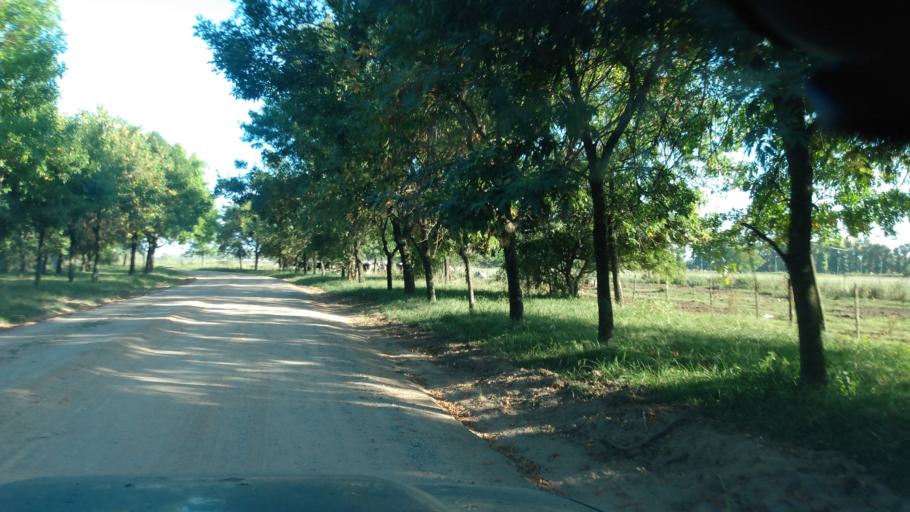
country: AR
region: Buenos Aires
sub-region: Partido de Lujan
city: Lujan
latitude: -34.5834
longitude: -59.0776
